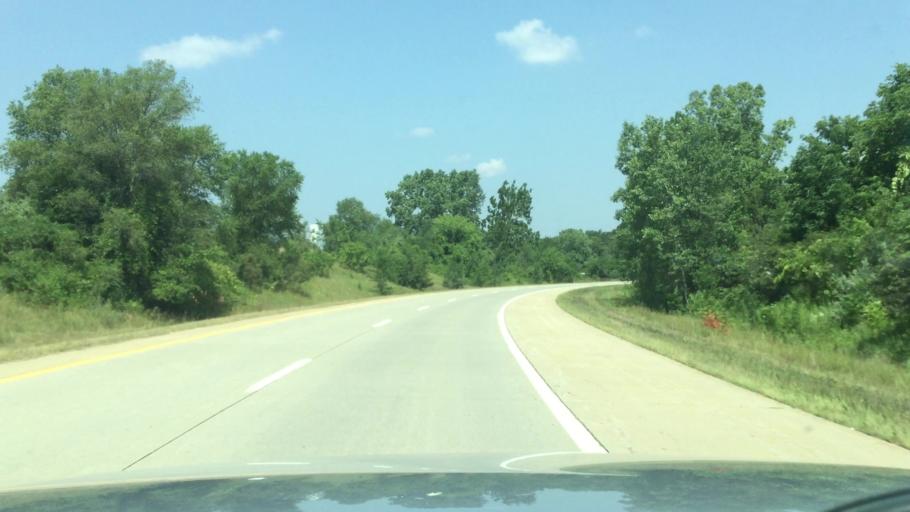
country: US
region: Michigan
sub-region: Washtenaw County
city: Ypsilanti
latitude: 42.2192
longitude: -83.5603
